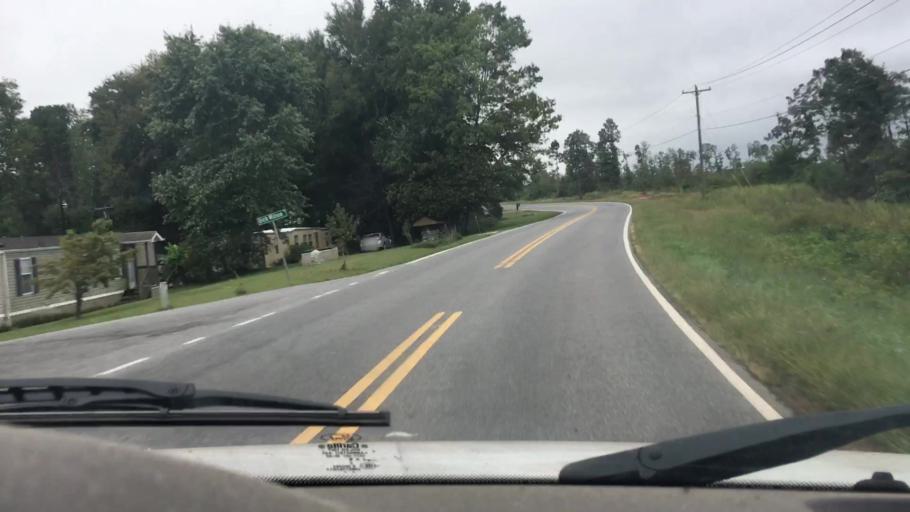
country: US
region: North Carolina
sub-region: Lincoln County
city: Denver
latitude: 35.5484
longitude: -81.0013
